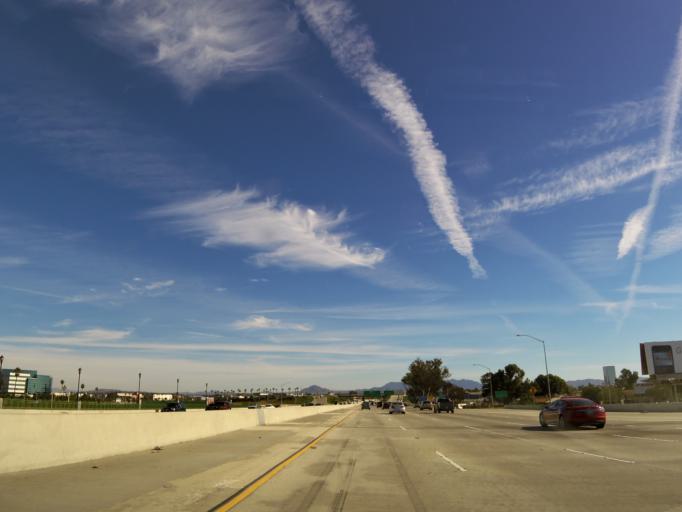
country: US
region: California
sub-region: Ventura County
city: El Rio
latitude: 34.2420
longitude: -119.1884
